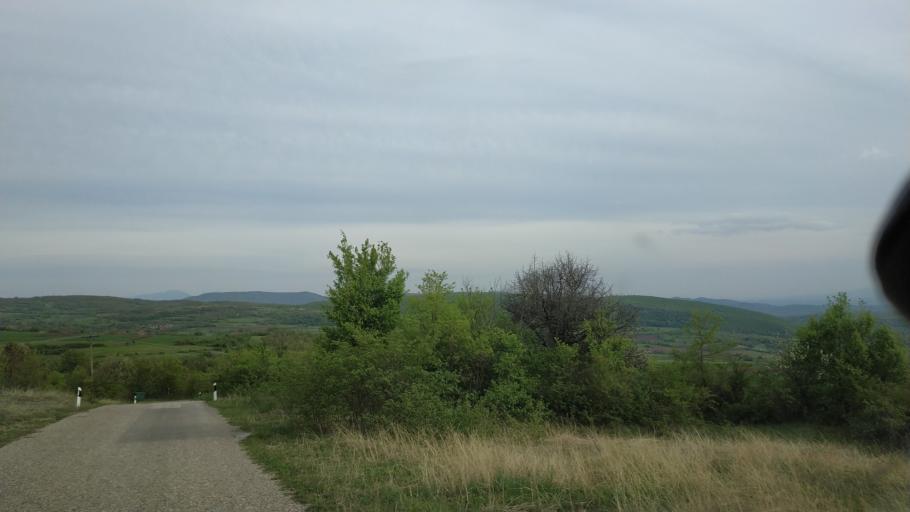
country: RS
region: Central Serbia
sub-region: Zajecarski Okrug
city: Soko Banja
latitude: 43.5316
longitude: 21.8777
